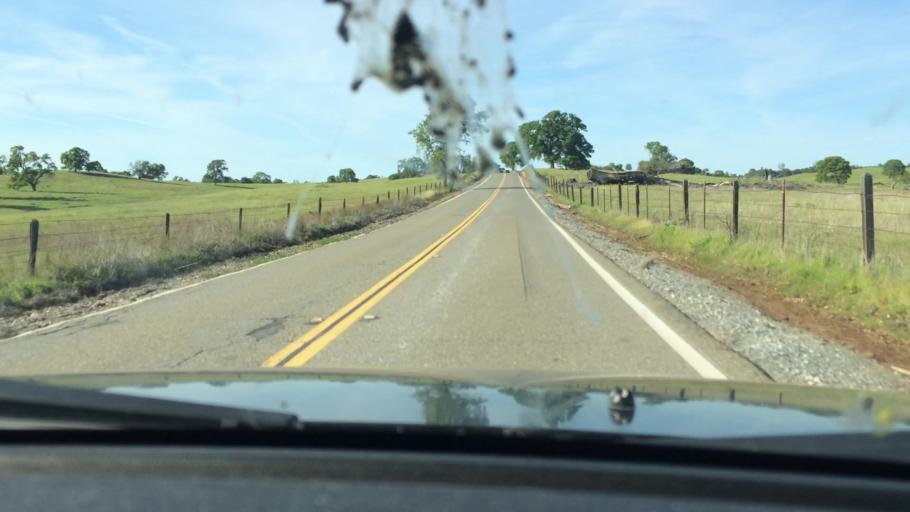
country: US
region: California
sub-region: Amador County
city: Plymouth
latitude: 38.4840
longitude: -120.9319
